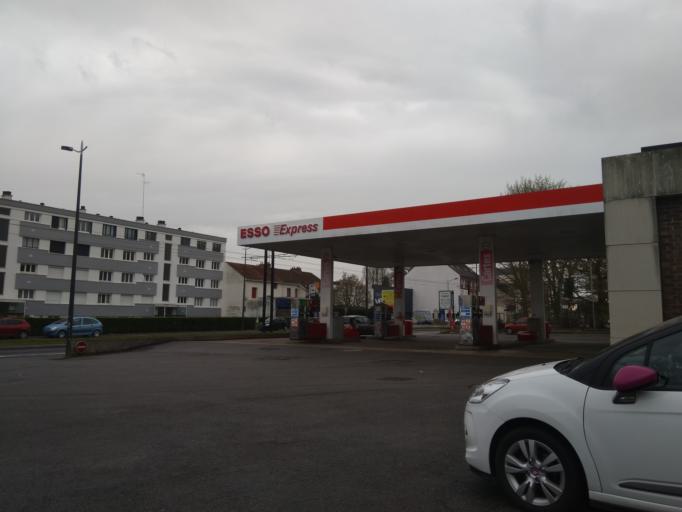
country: FR
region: Pays de la Loire
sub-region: Departement de la Loire-Atlantique
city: Nantes
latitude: 47.2397
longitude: -1.5896
